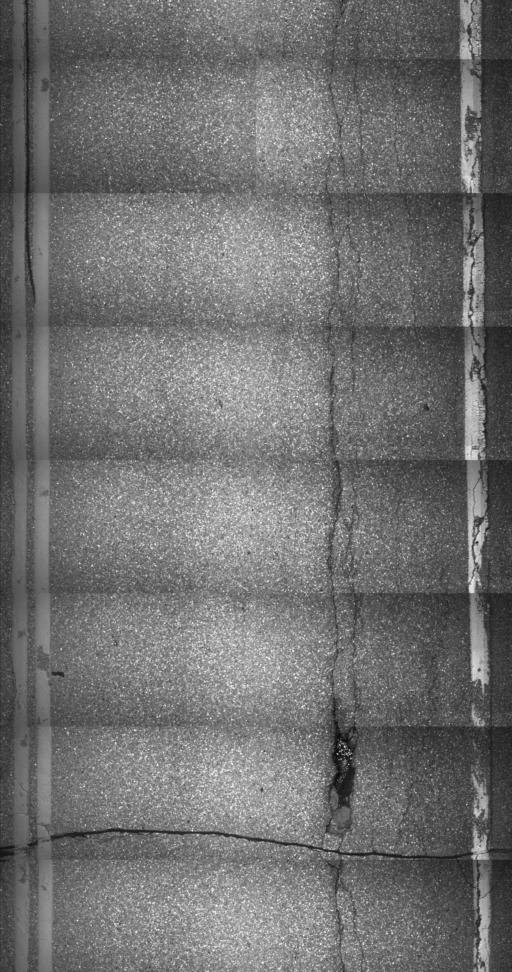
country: US
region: Vermont
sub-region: Chittenden County
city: Milton
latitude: 44.7156
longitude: -73.1055
